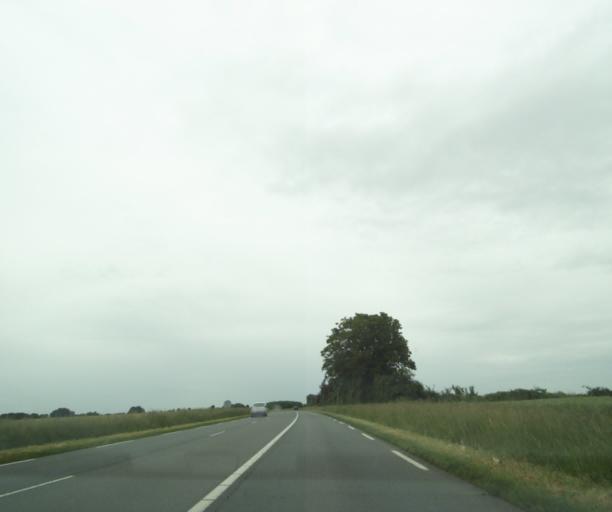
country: FR
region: Poitou-Charentes
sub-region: Departement des Deux-Sevres
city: Cherveux
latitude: 46.4332
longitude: -0.3906
